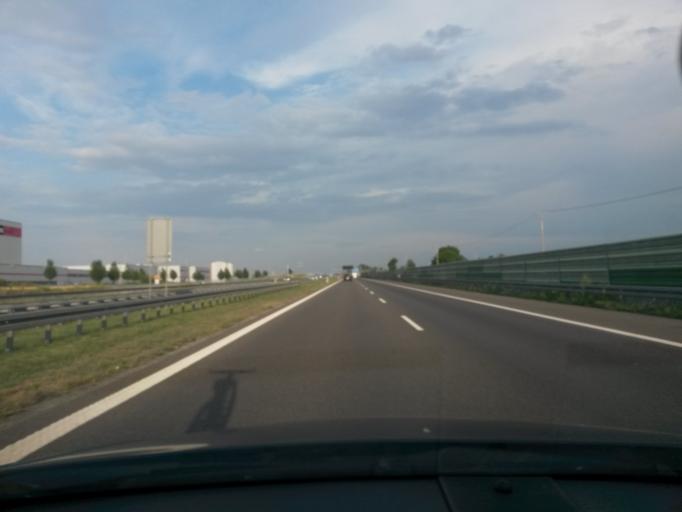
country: PL
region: Lodz Voivodeship
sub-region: Powiat zgierski
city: Strykow
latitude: 51.8911
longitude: 19.5662
